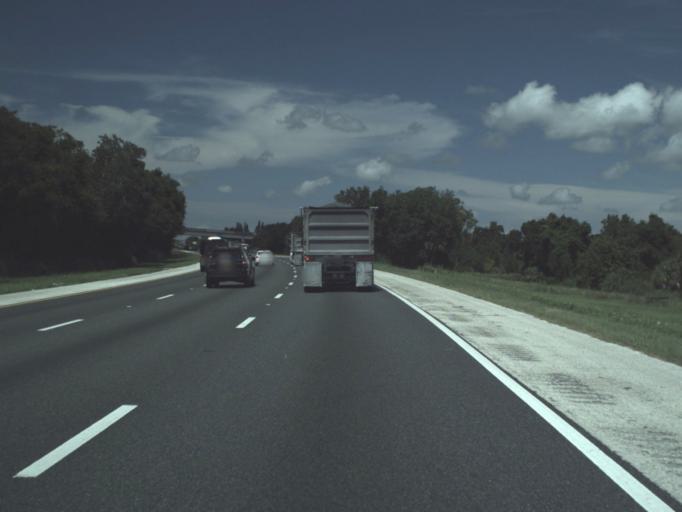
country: US
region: Florida
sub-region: Manatee County
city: Ellenton
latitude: 27.5014
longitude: -82.4783
